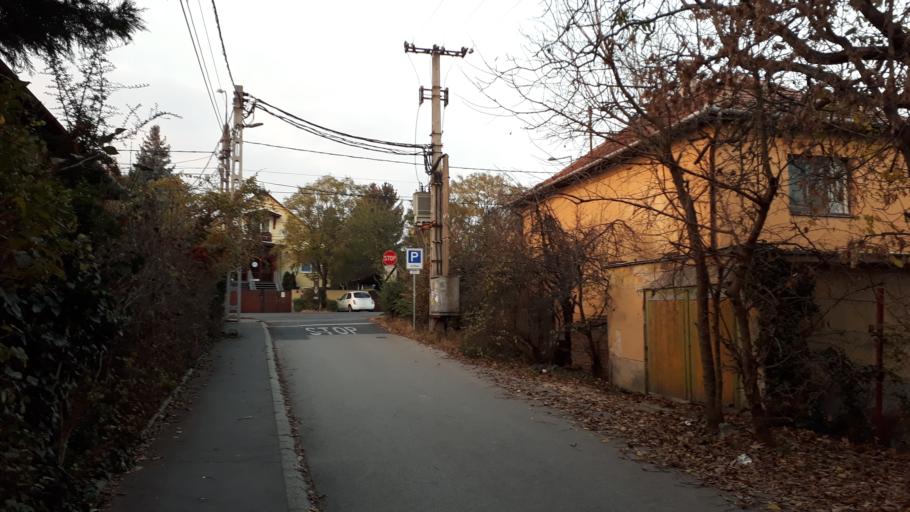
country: HU
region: Pest
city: Budaors
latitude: 47.4623
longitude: 18.9773
